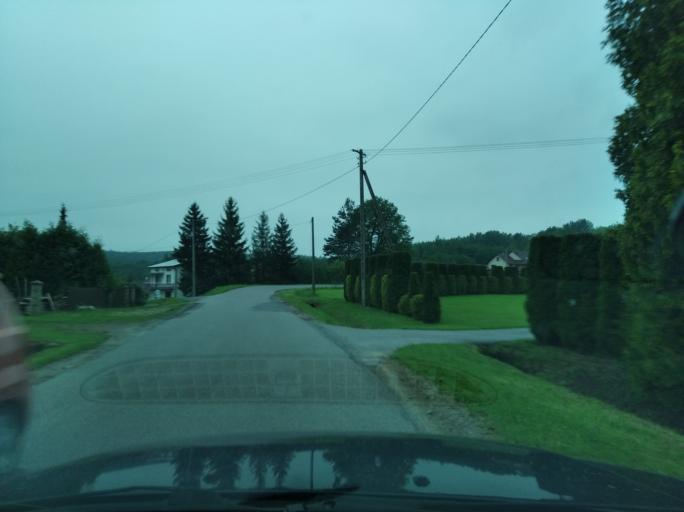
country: PL
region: Subcarpathian Voivodeship
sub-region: Powiat brzozowski
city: Orzechowka
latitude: 49.7284
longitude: 21.9358
